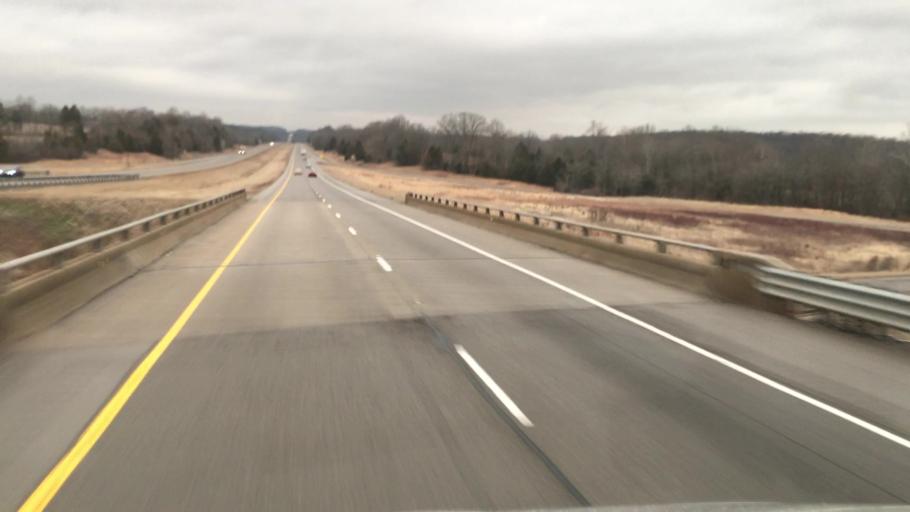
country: US
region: Illinois
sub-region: Johnson County
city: Vienna
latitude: 37.4464
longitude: -88.8867
